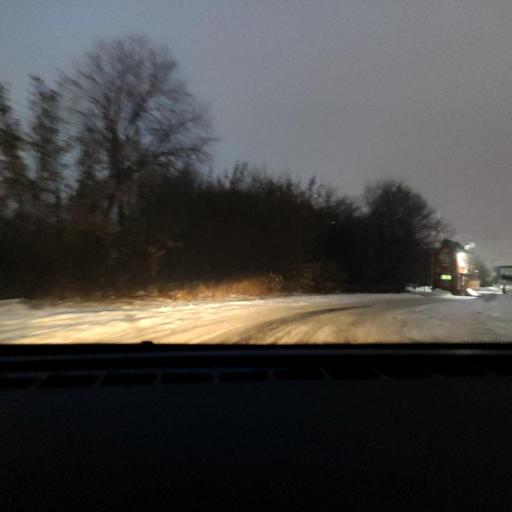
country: RU
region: Voronezj
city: Voronezh
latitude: 51.6483
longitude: 39.2644
